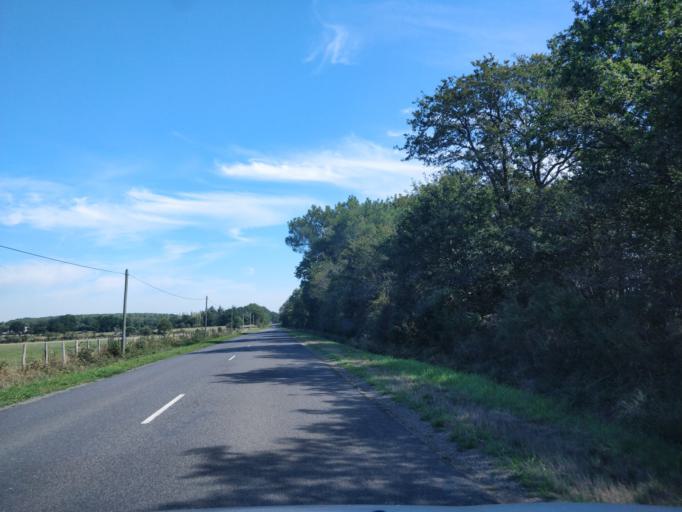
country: FR
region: Pays de la Loire
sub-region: Departement de la Loire-Atlantique
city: Quilly
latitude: 47.4759
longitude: -1.9186
